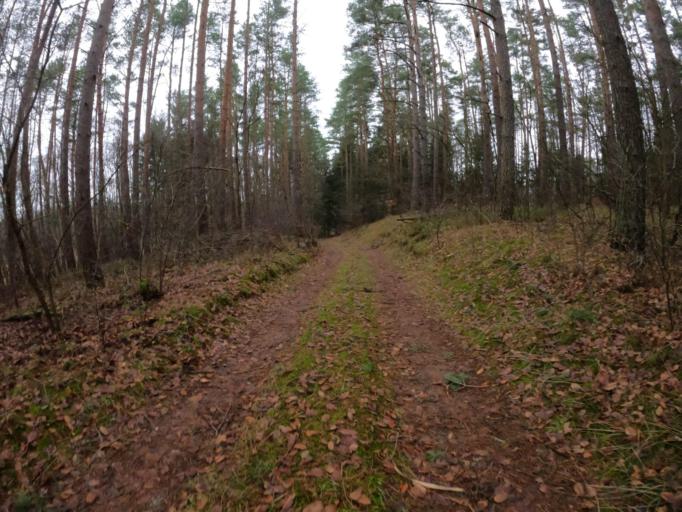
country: PL
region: West Pomeranian Voivodeship
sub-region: Powiat mysliborski
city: Debno
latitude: 52.7311
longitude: 14.7551
